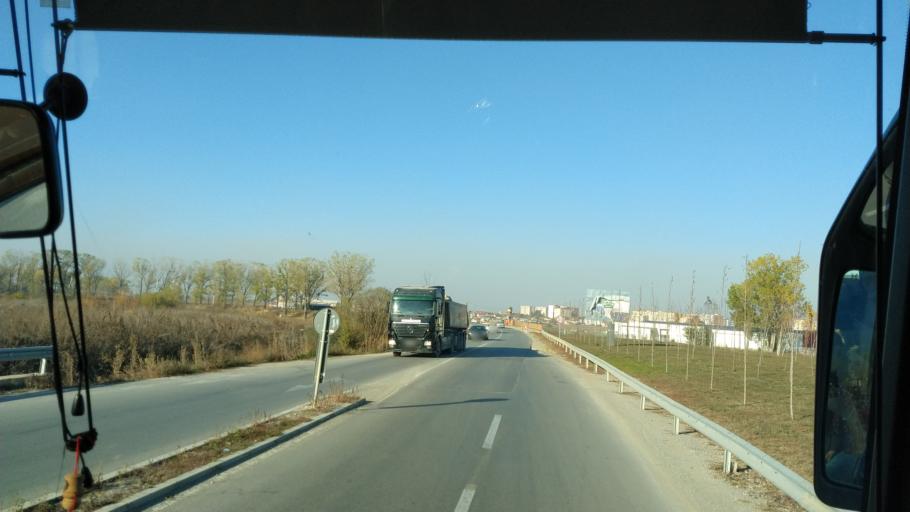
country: XK
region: Pristina
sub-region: Lipjan
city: Lipljan
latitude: 42.5117
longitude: 21.1128
